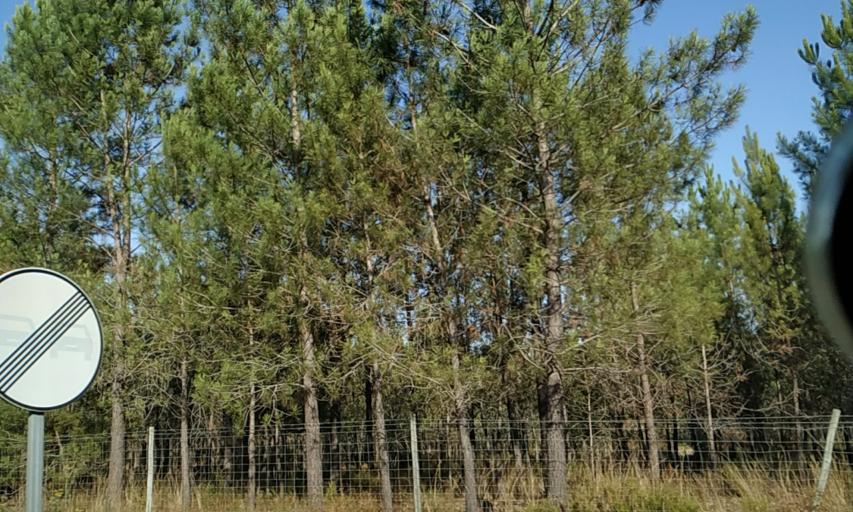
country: PT
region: Santarem
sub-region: Coruche
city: Coruche
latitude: 39.0314
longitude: -8.5615
